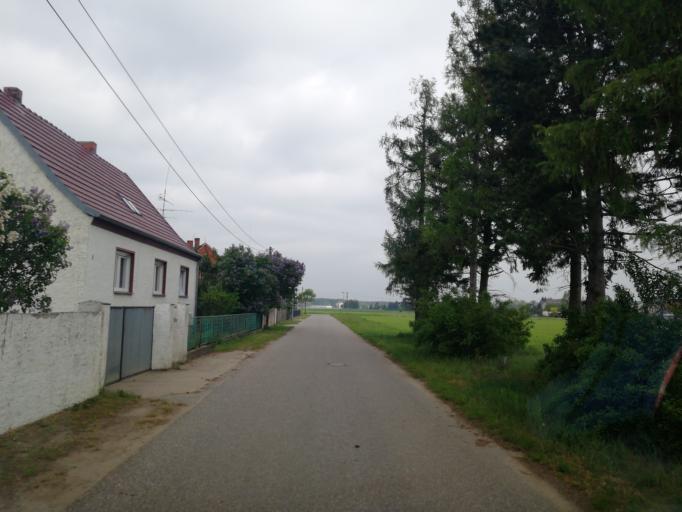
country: DE
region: Saxony
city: Beilrode
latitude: 51.6419
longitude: 13.1165
